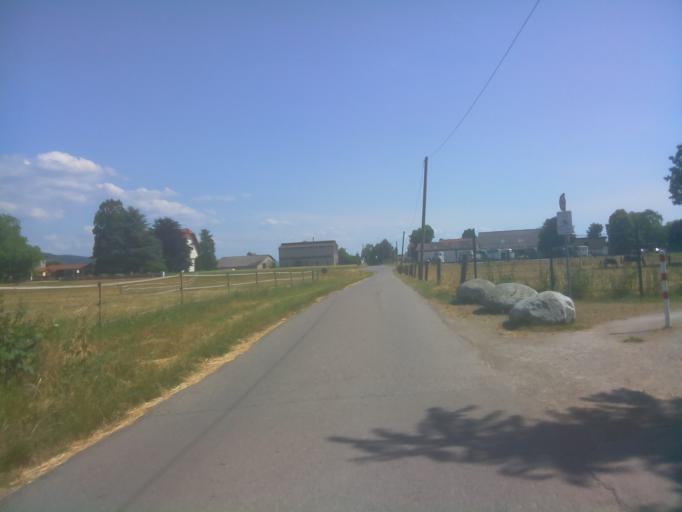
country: DE
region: Baden-Wuerttemberg
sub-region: Karlsruhe Region
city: Heddesheim
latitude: 49.5208
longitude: 8.6244
